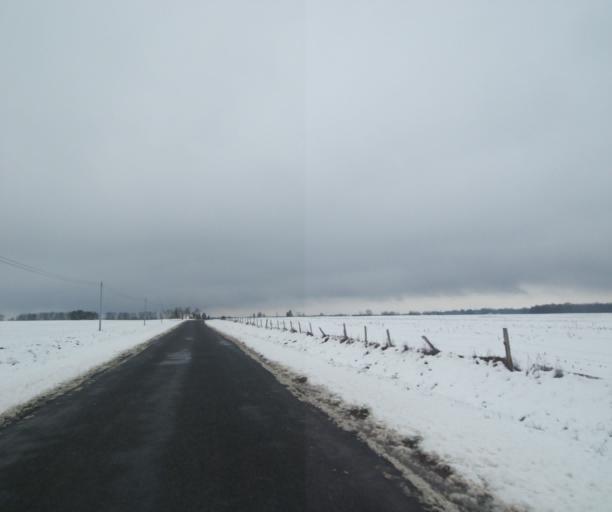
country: FR
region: Champagne-Ardenne
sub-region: Departement de la Haute-Marne
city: Laneuville-a-Remy
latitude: 48.4998
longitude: 4.8686
